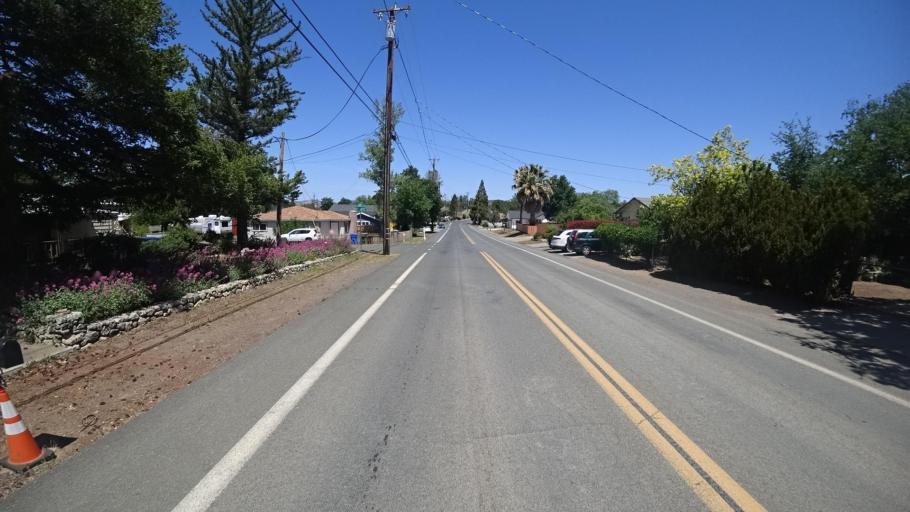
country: US
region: California
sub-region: Lake County
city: Lower Lake
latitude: 38.9122
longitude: -122.6093
